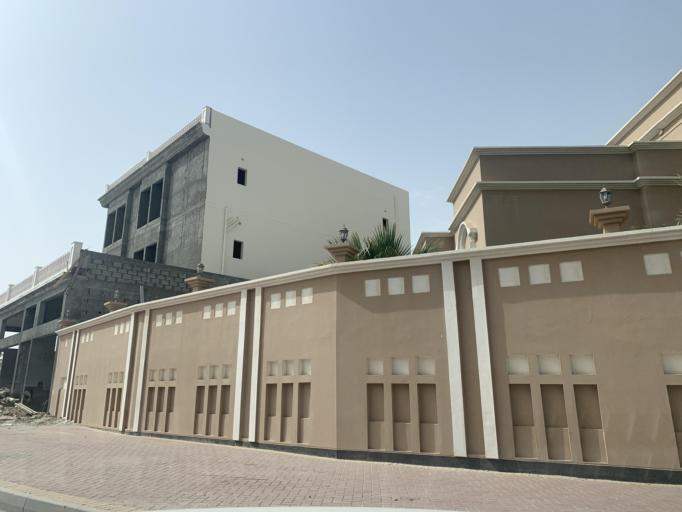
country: BH
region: Central Governorate
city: Madinat Hamad
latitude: 26.1444
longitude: 50.5143
